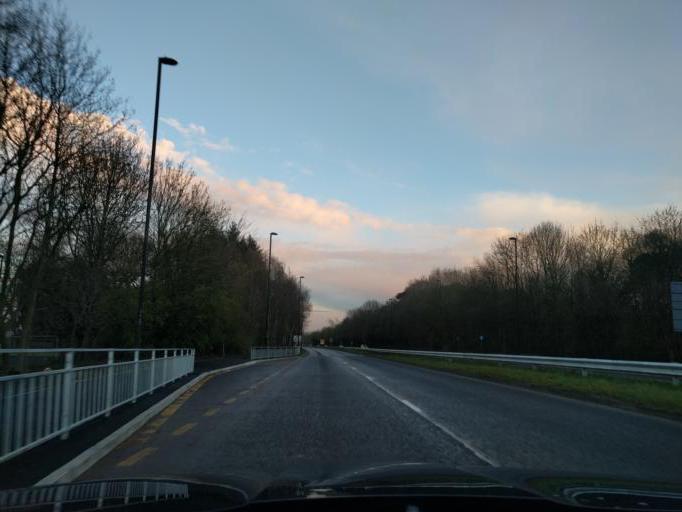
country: GB
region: England
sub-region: Newcastle upon Tyne
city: Gosforth
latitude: 55.0312
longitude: -1.5904
